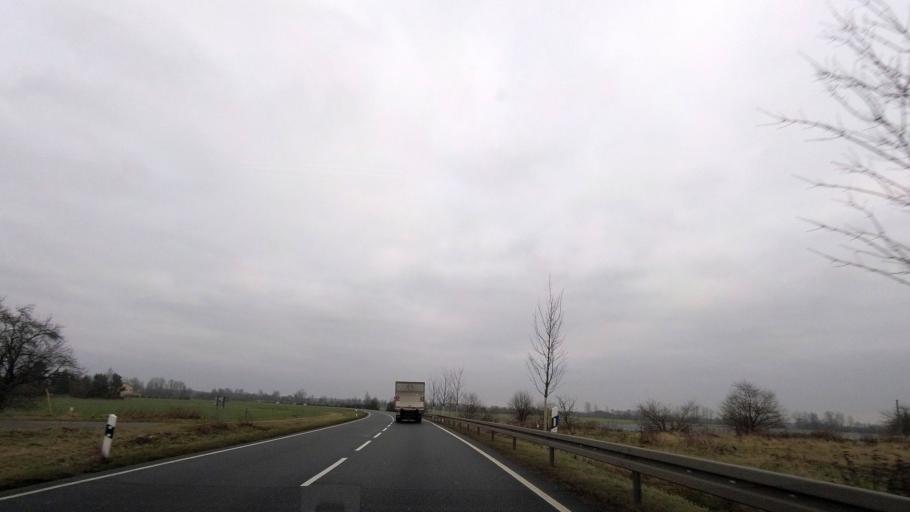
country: DE
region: Brandenburg
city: Beelitz
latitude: 52.2243
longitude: 12.9787
